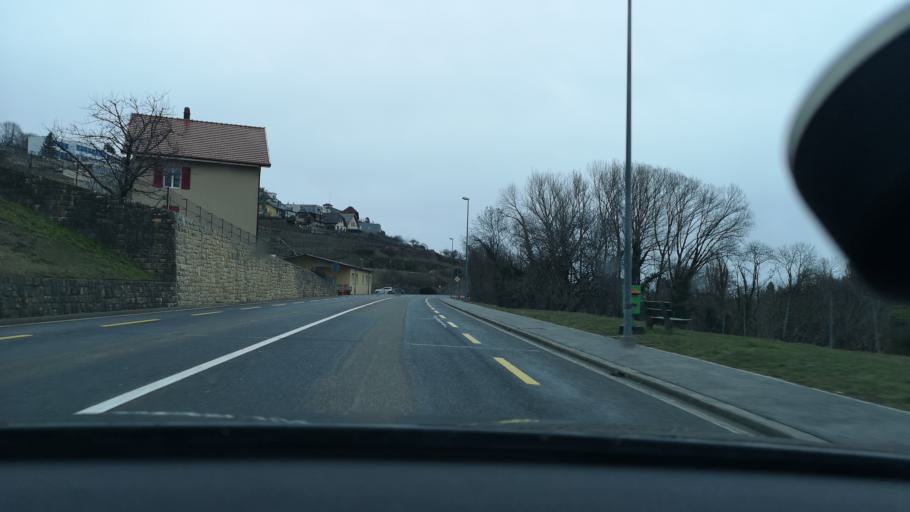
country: CH
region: Neuchatel
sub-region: Boudry District
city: Saint-Aubin-Sauges
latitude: 46.8898
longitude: 6.7679
